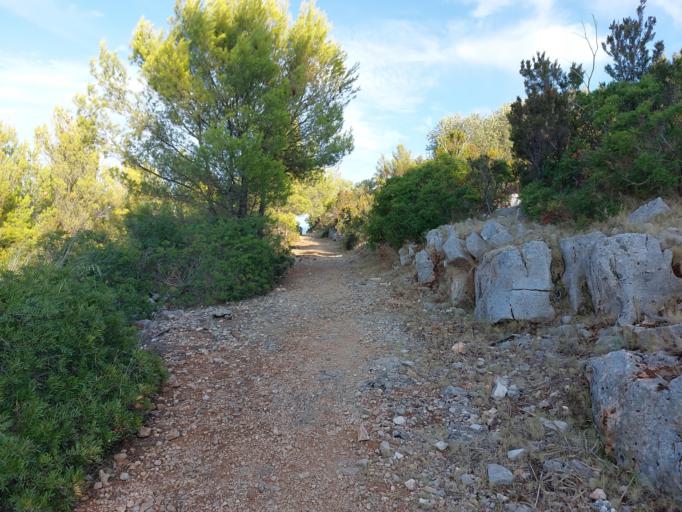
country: HR
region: Dubrovacko-Neretvanska
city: Smokvica
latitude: 42.7287
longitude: 16.8431
